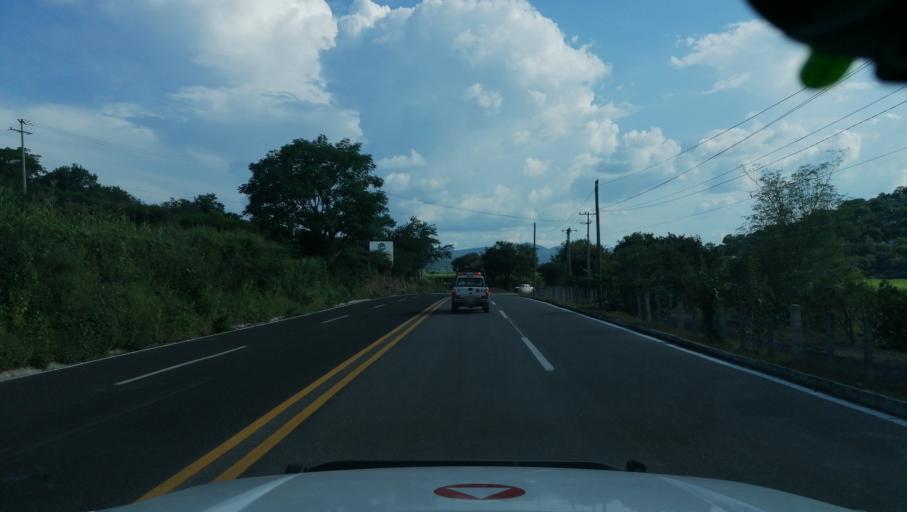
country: MX
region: Morelos
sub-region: Ayala
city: El Salitre
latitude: 18.6961
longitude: -98.9929
